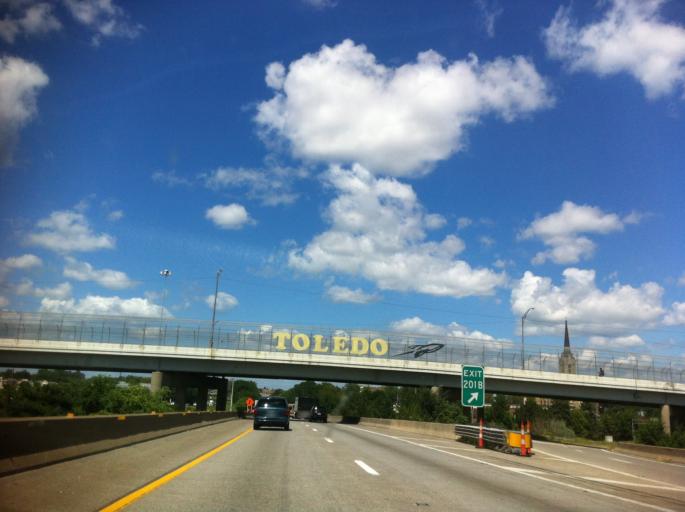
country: US
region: Ohio
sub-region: Lucas County
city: Toledo
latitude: 41.6449
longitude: -83.5486
